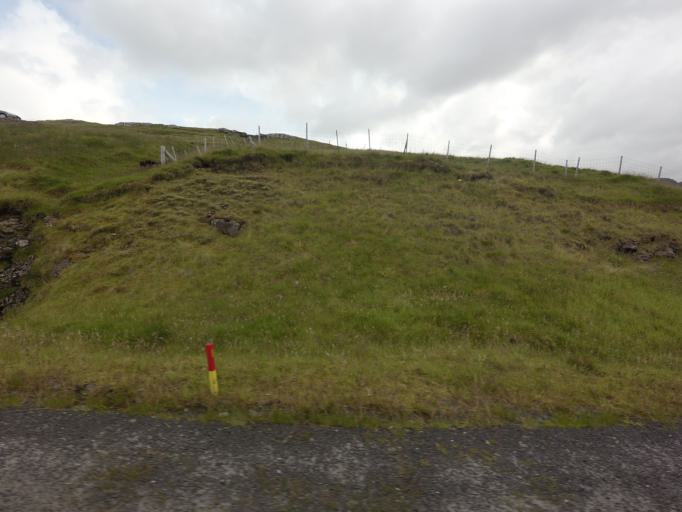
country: FO
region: Eysturoy
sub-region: Eidi
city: Eidi
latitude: 62.2217
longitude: -7.0033
